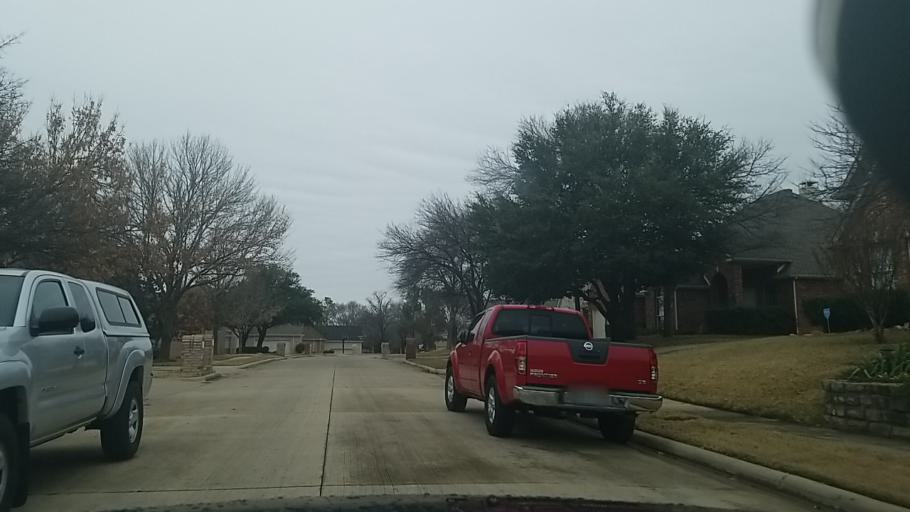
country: US
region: Texas
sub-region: Denton County
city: Corinth
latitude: 33.1564
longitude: -97.0781
